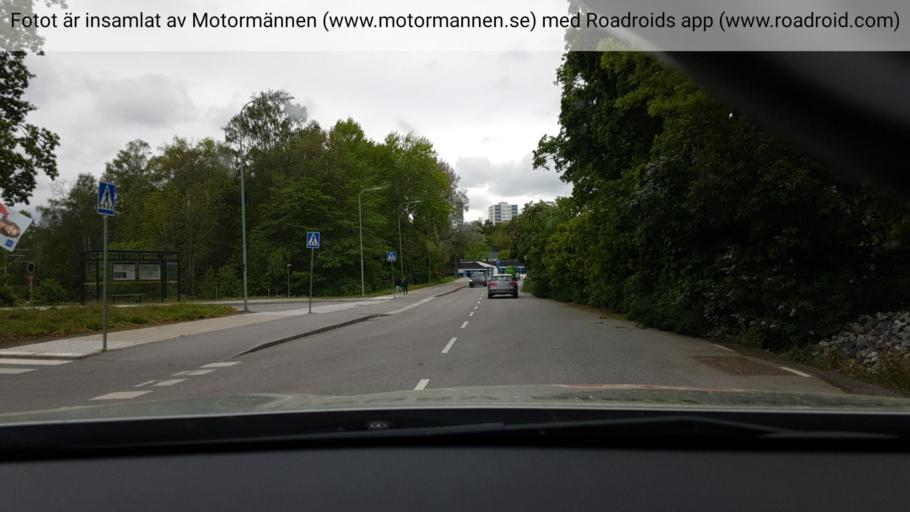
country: SE
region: Stockholm
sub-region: Lidingo
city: Brevik
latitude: 59.3446
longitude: 18.1802
